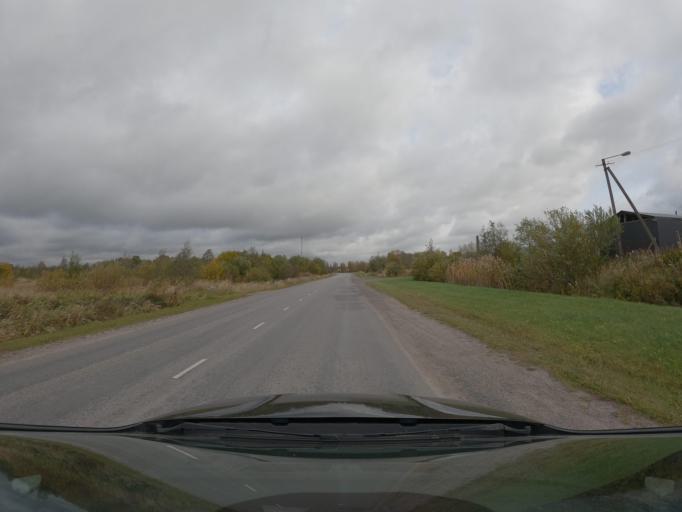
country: EE
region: Saare
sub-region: Kuressaare linn
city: Kuressaare
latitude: 58.2665
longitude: 22.4843
